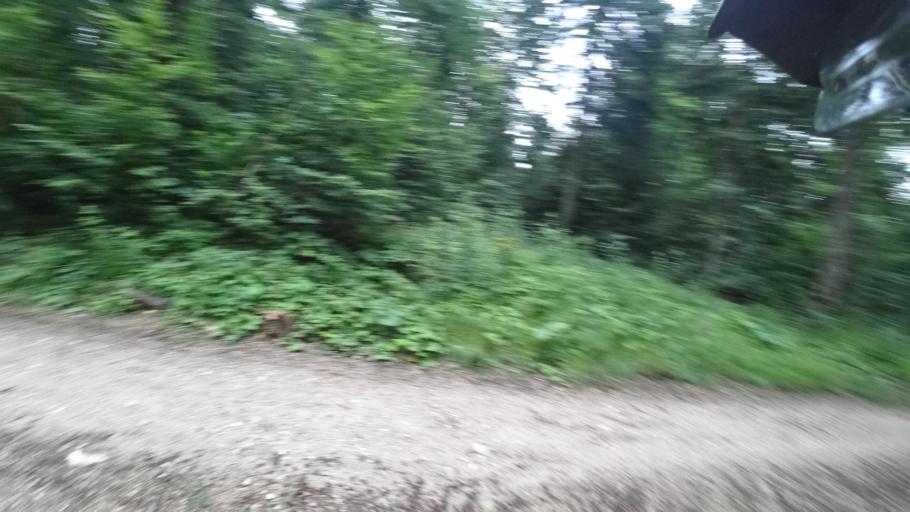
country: BA
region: Federation of Bosnia and Herzegovina
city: Orasac
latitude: 44.4970
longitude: 15.9407
